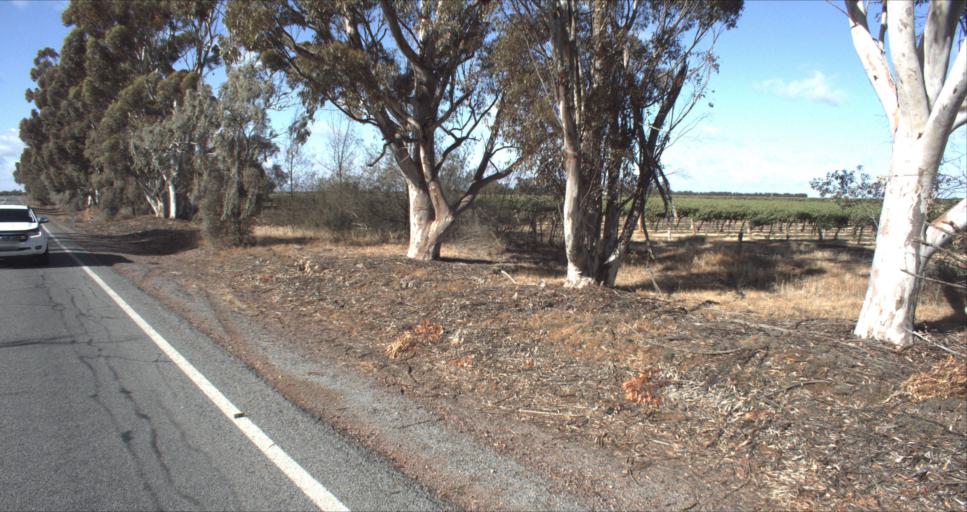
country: AU
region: New South Wales
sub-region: Leeton
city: Leeton
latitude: -34.5465
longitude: 146.3544
